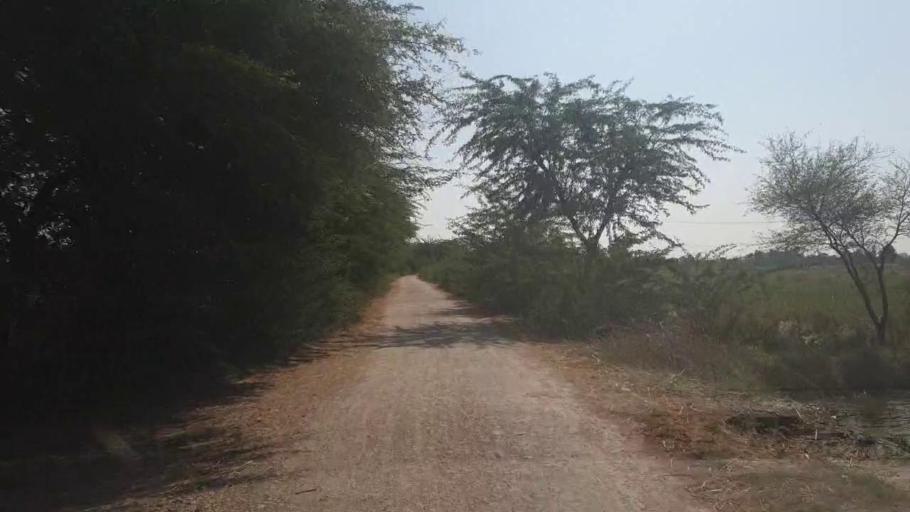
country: PK
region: Sindh
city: Badin
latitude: 24.6339
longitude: 68.9124
